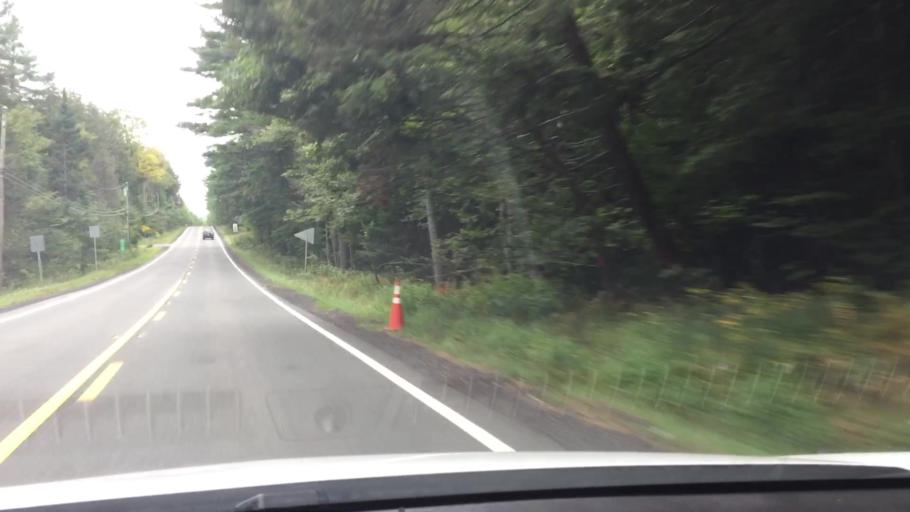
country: US
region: Massachusetts
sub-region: Berkshire County
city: Becket
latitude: 42.3536
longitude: -73.0958
